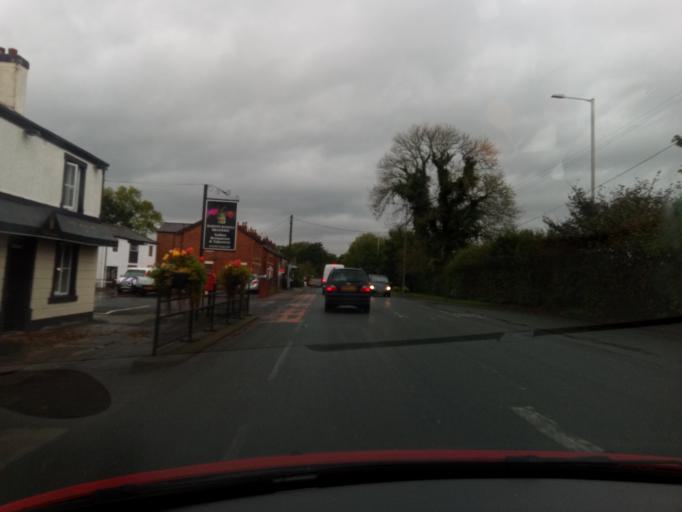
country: GB
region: England
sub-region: Lancashire
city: Catterall
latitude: 53.8381
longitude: -2.7395
